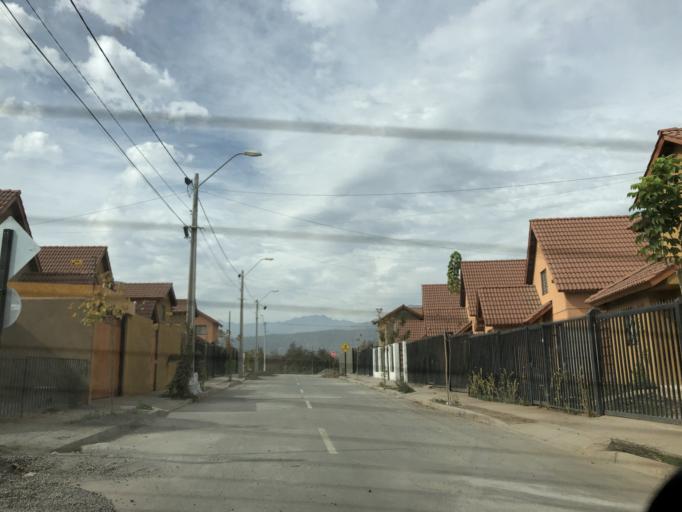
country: CL
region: Santiago Metropolitan
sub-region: Provincia de Cordillera
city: Puente Alto
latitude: -33.5851
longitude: -70.5300
